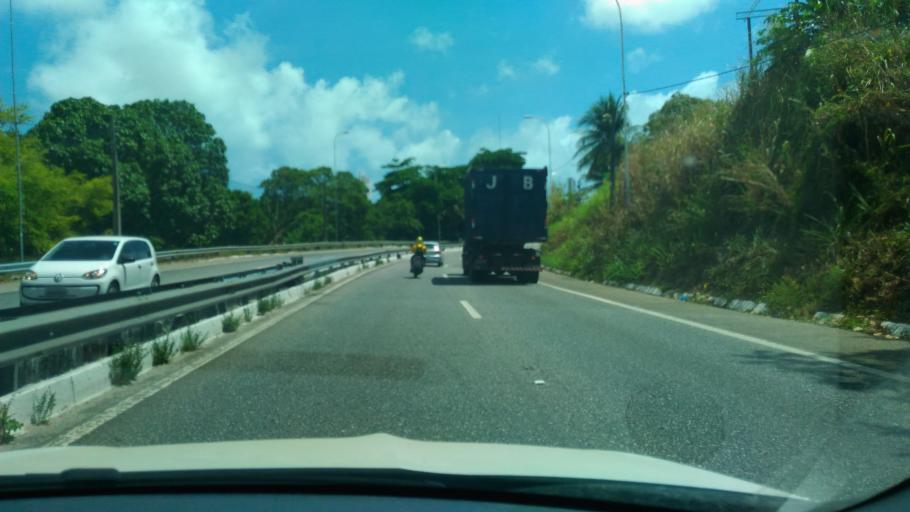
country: BR
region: Paraiba
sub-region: Joao Pessoa
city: Joao Pessoa
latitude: -7.1294
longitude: -34.8503
